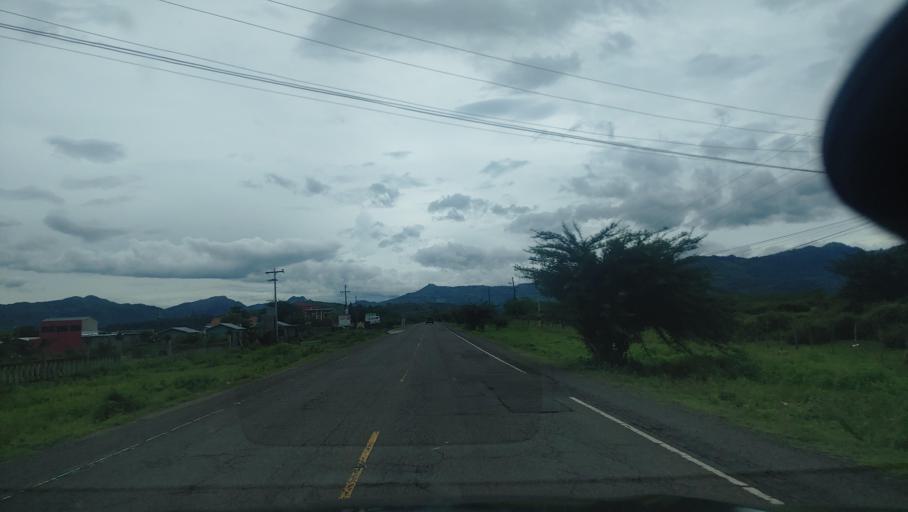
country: HN
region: Choluteca
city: Santa Ana de Yusguare
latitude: 13.3462
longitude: -87.1176
